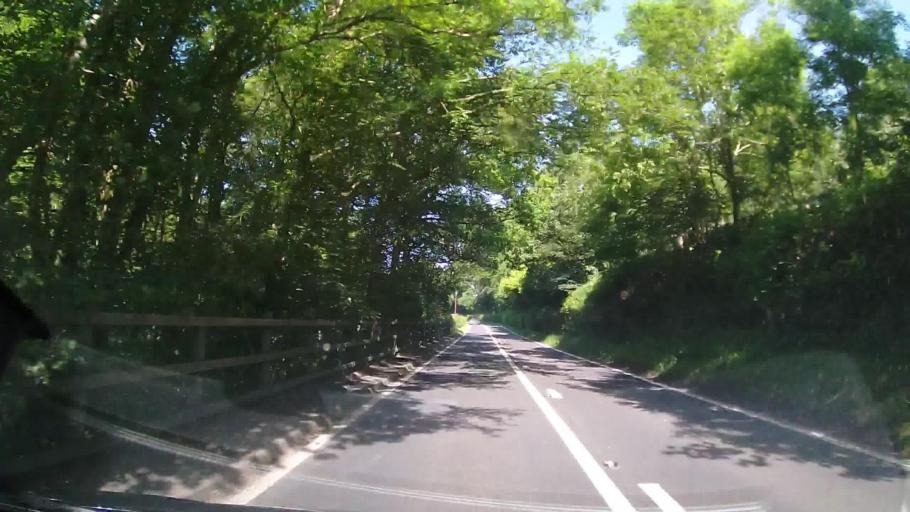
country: GB
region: Wales
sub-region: Sir Powys
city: Llanfyllin
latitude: 52.6513
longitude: -3.3372
